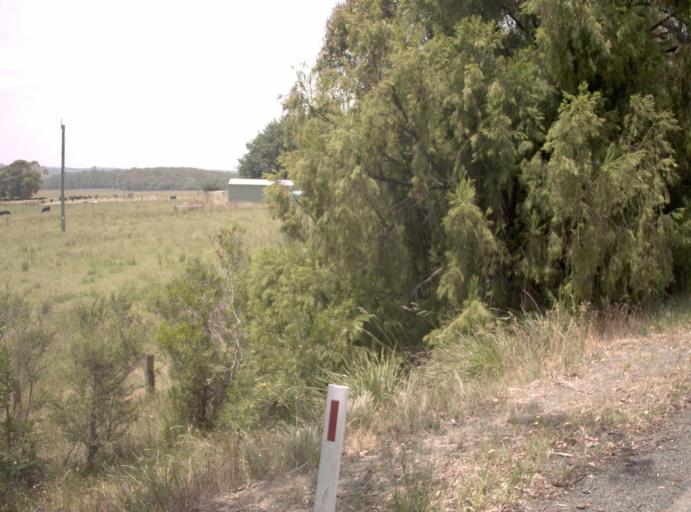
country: AU
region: Victoria
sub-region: Latrobe
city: Traralgon
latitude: -38.3806
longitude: 146.7587
